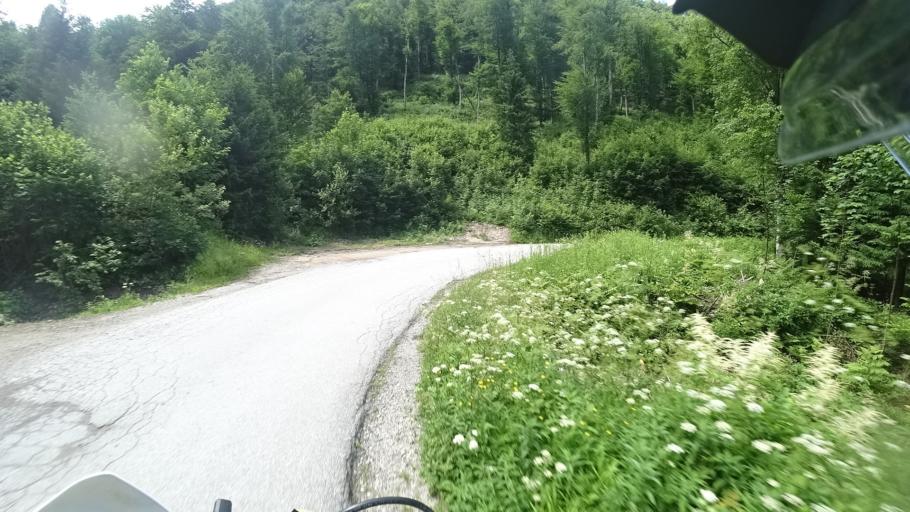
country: SI
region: Osilnica
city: Osilnica
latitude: 45.5041
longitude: 14.6280
